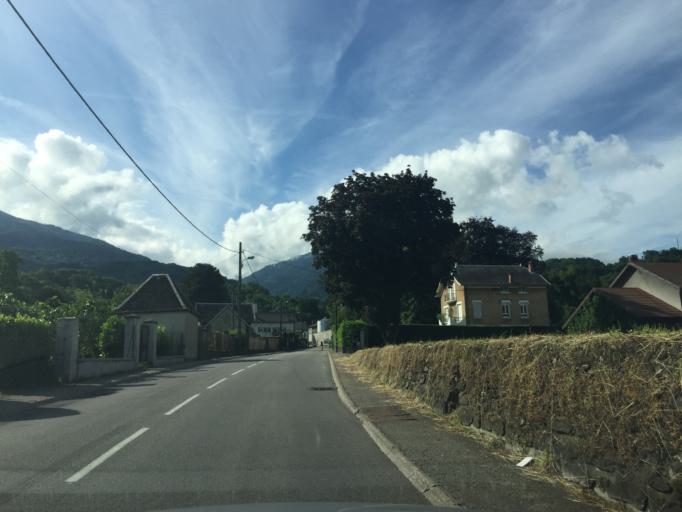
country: FR
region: Rhone-Alpes
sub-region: Departement de la Savoie
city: La Rochette
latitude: 45.4555
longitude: 6.1172
